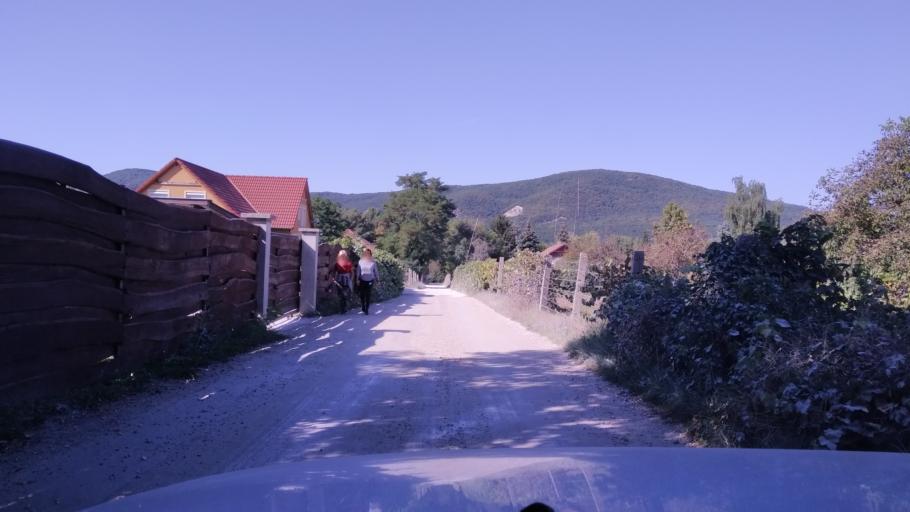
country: HU
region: Komarom-Esztergom
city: Esztergom
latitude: 47.8125
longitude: 18.7864
